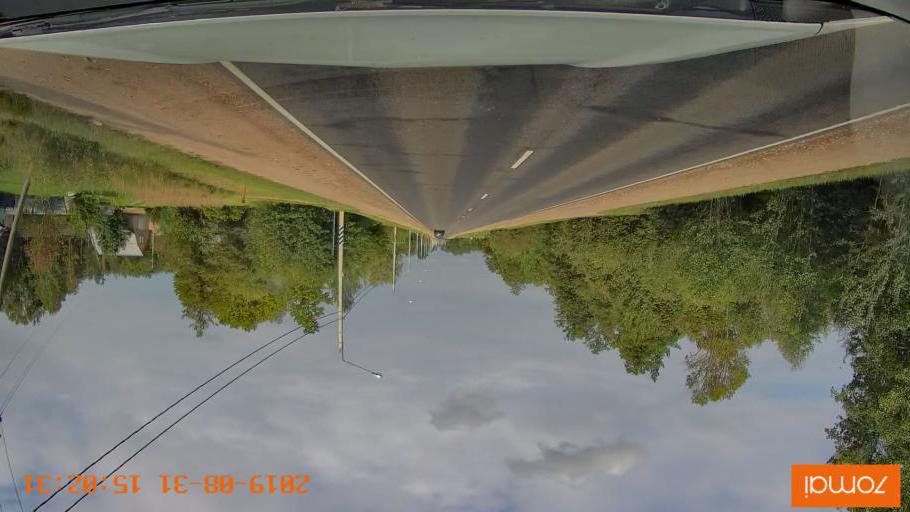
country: RU
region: Kaluga
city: Spas-Demensk
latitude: 54.3462
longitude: 34.0757
